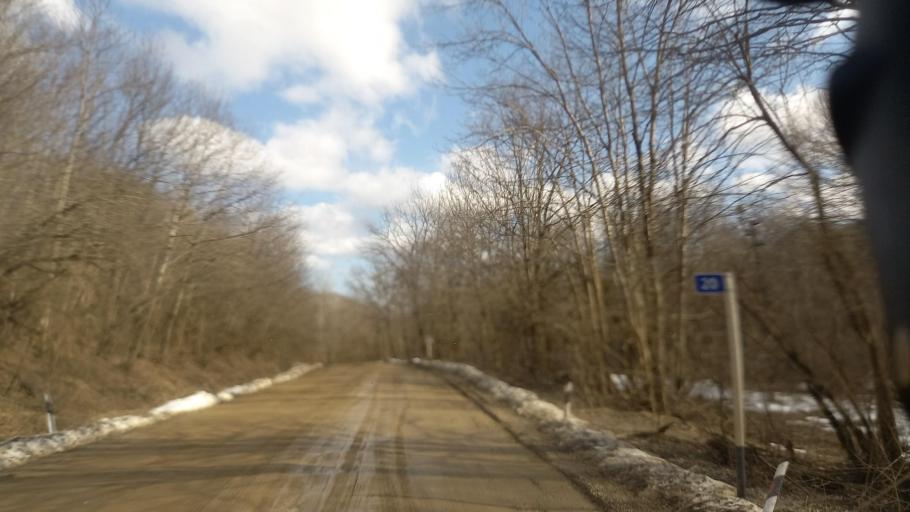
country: RU
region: Krasnodarskiy
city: Smolenskaya
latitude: 44.6057
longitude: 38.7792
